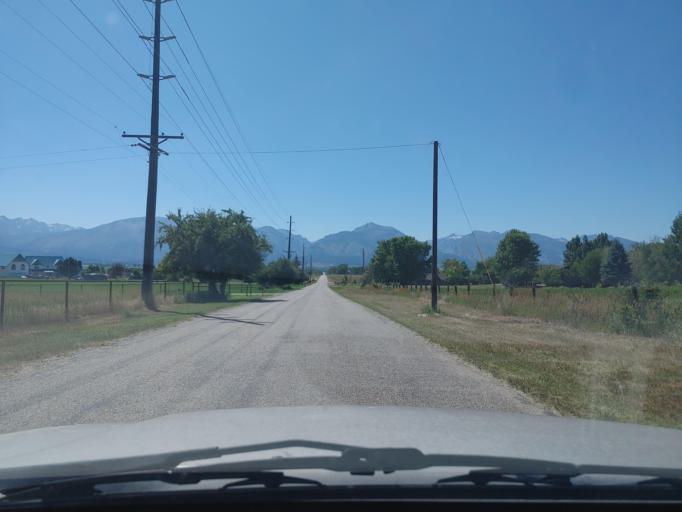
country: US
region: Montana
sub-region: Ravalli County
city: Hamilton
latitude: 46.2768
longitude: -114.0569
